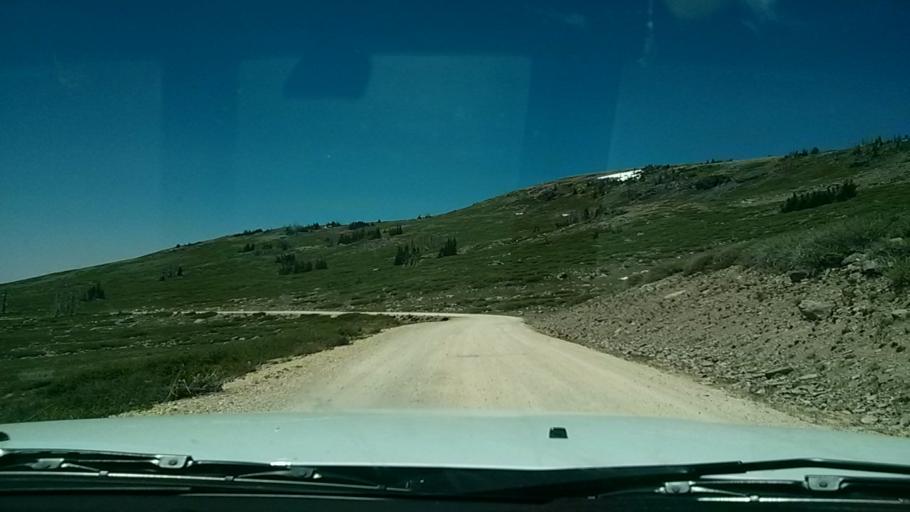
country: US
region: Utah
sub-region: Iron County
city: Parowan
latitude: 37.6812
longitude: -112.8213
